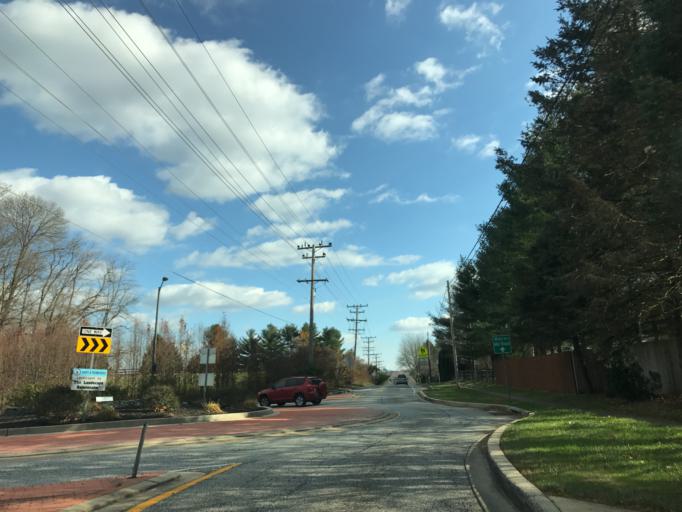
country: US
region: Maryland
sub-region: Harford County
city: South Bel Air
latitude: 39.5484
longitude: -76.3354
